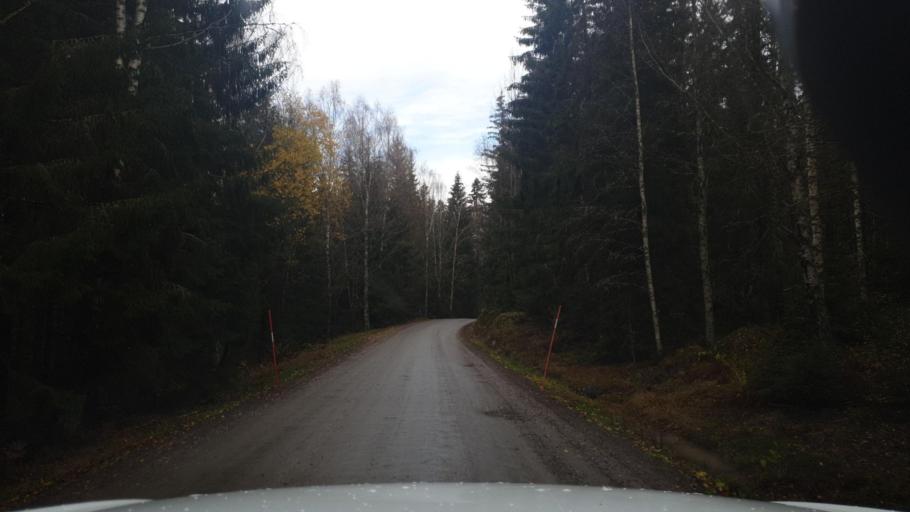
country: NO
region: Ostfold
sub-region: Romskog
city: Romskog
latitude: 59.8256
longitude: 11.9979
